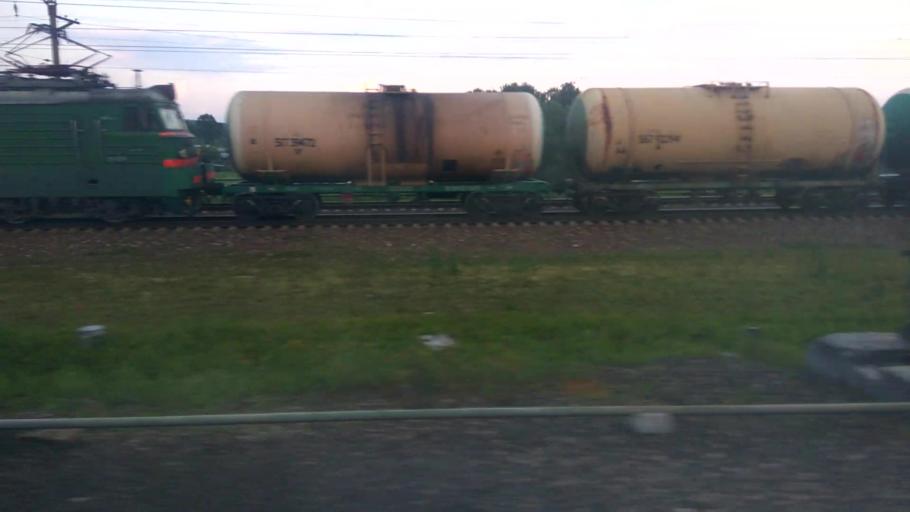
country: RU
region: Moskovskaya
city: Mikhnevo
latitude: 55.1288
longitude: 37.9585
